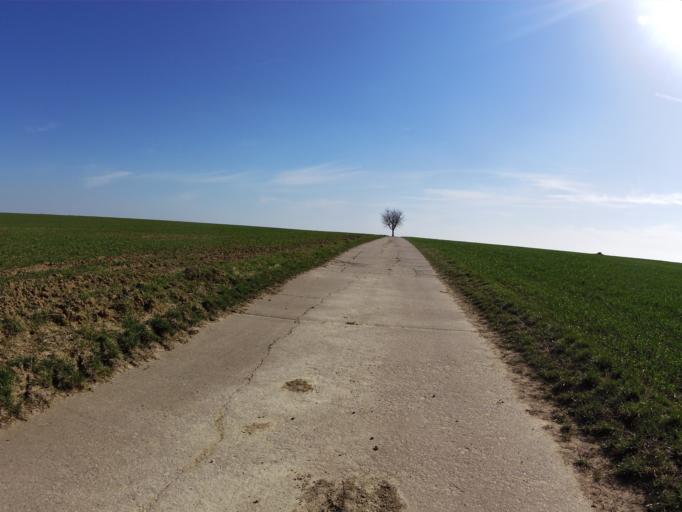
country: DE
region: Bavaria
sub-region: Regierungsbezirk Unterfranken
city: Prosselsheim
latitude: 49.8524
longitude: 10.1211
